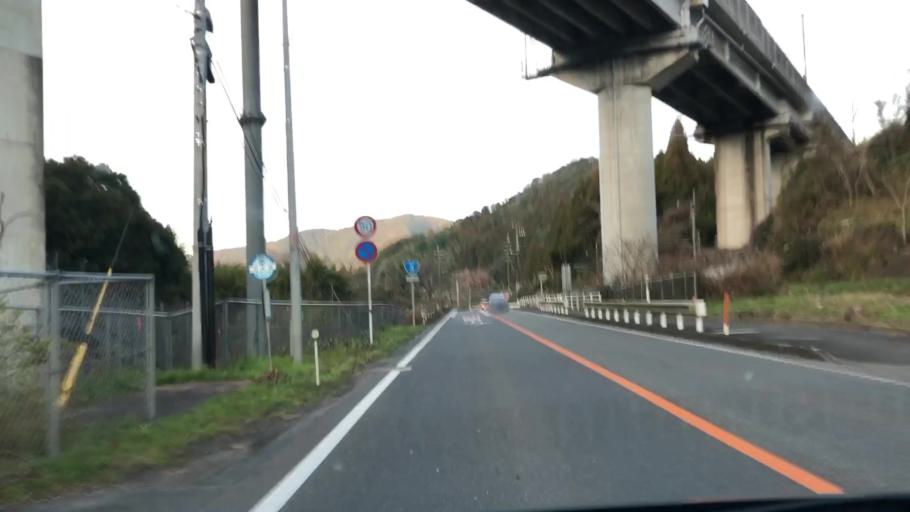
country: JP
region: Kumamoto
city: Minamata
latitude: 32.2177
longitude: 130.4377
